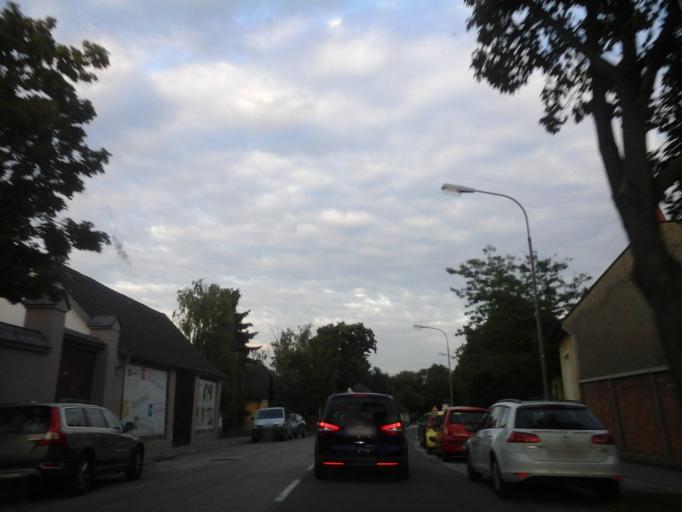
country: AT
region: Lower Austria
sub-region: Politischer Bezirk Wien-Umgebung
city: Schwechat
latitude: 48.1461
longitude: 16.5199
